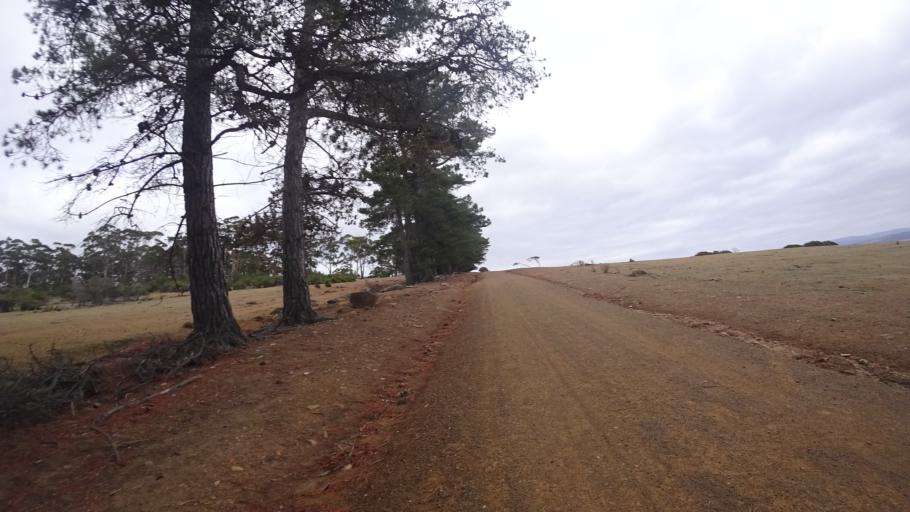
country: AU
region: Tasmania
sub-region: Sorell
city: Sorell
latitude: -42.5831
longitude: 148.0622
